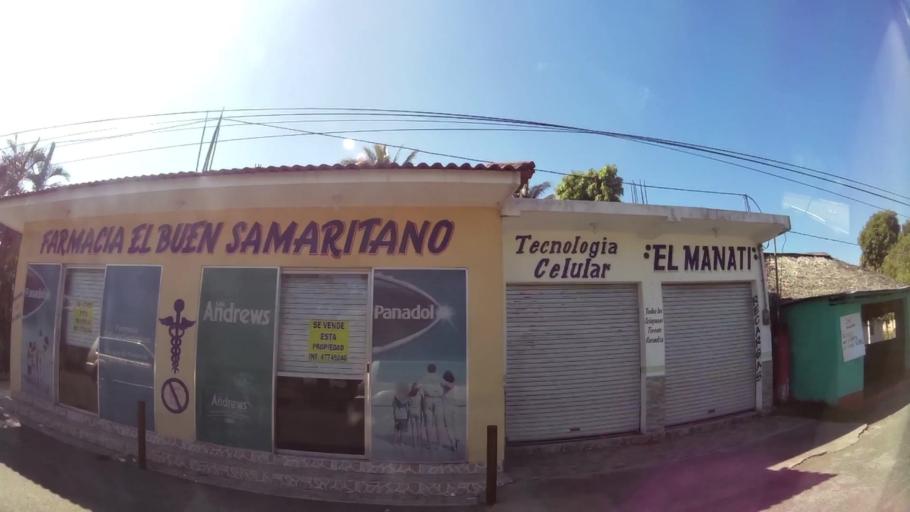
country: GT
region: Escuintla
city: Iztapa
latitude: 13.9166
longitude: -90.5507
